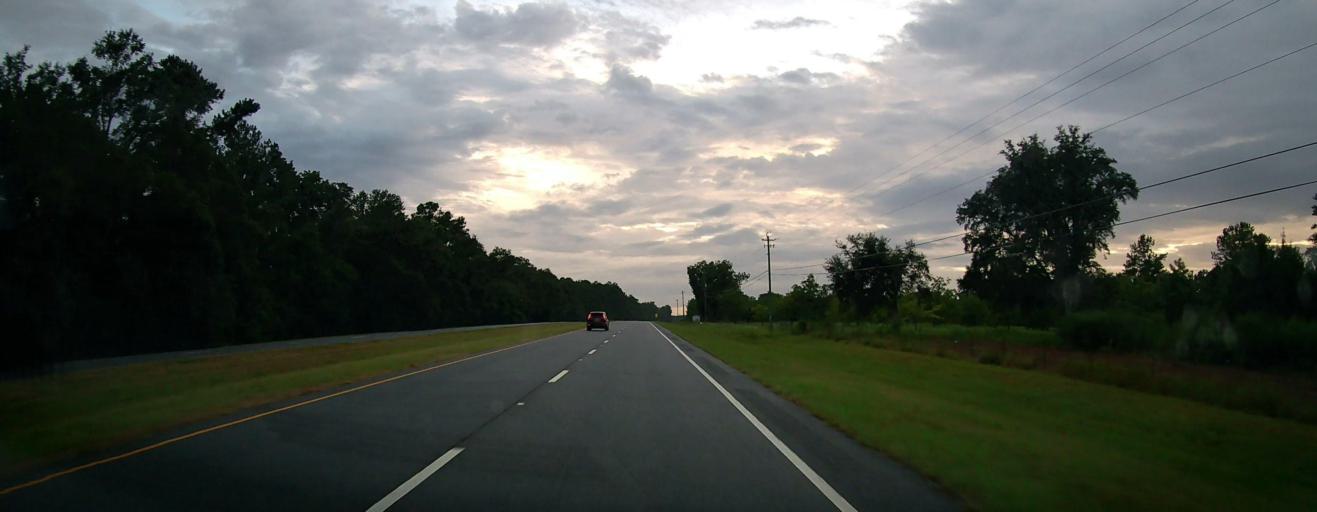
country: US
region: Georgia
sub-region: Lanier County
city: Lakeland
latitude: 30.9188
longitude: -83.0521
